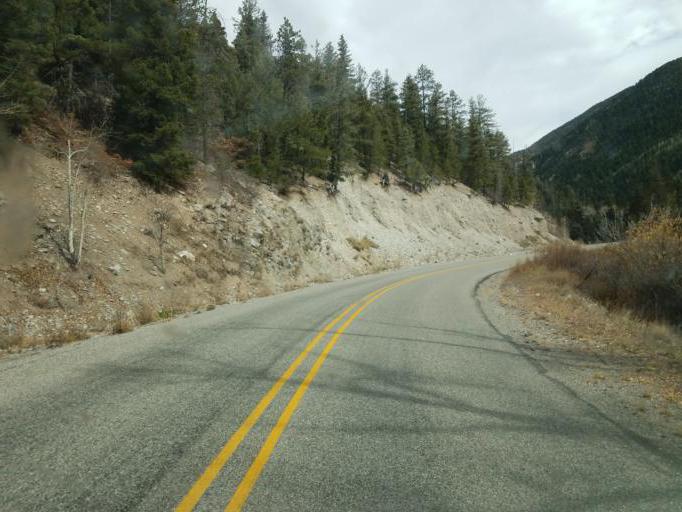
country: US
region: New Mexico
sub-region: Taos County
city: Arroyo Seco
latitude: 36.5732
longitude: -105.5153
